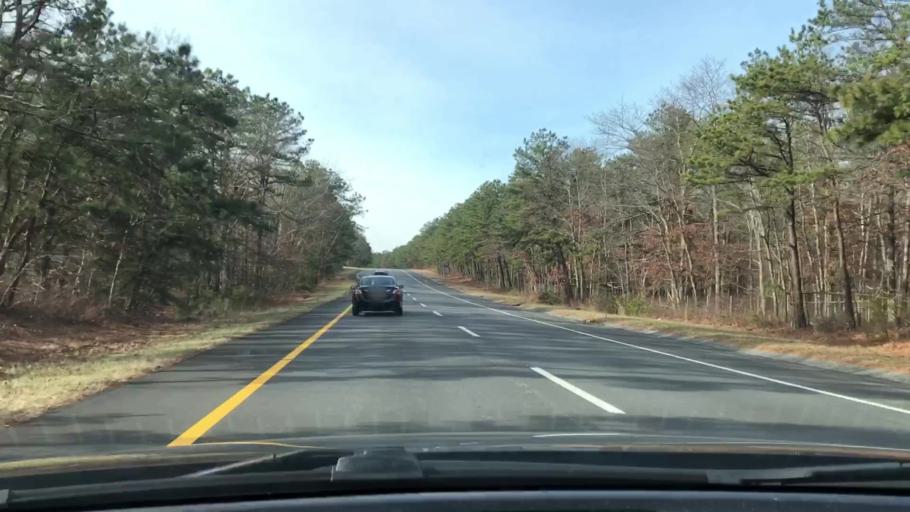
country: US
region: New York
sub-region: Suffolk County
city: Calverton
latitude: 40.9053
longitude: -72.7219
